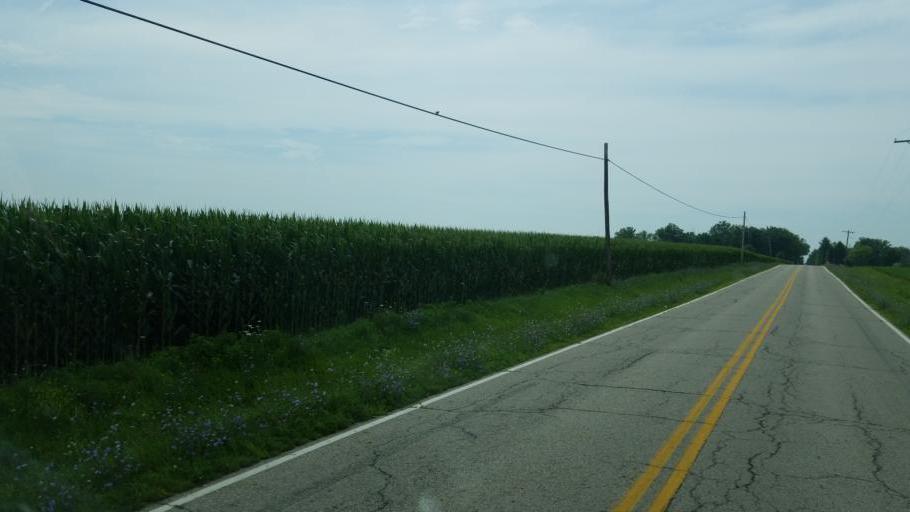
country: US
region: Ohio
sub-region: Madison County
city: Choctaw Lake
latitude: 39.9979
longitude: -83.3916
